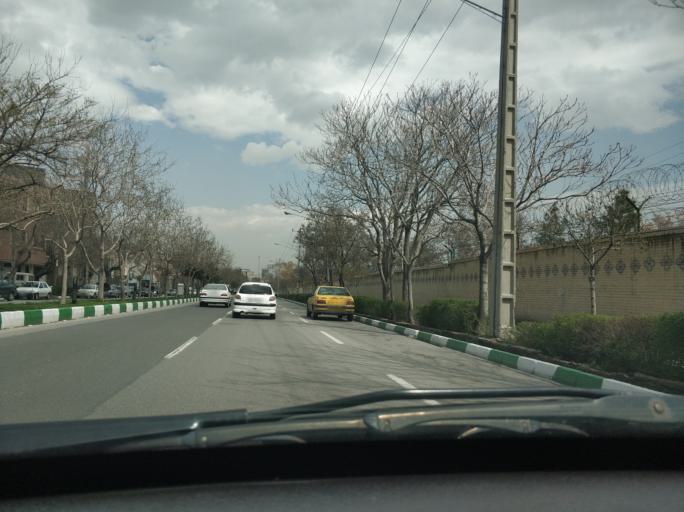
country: IR
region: Razavi Khorasan
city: Mashhad
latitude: 36.2816
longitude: 59.5776
